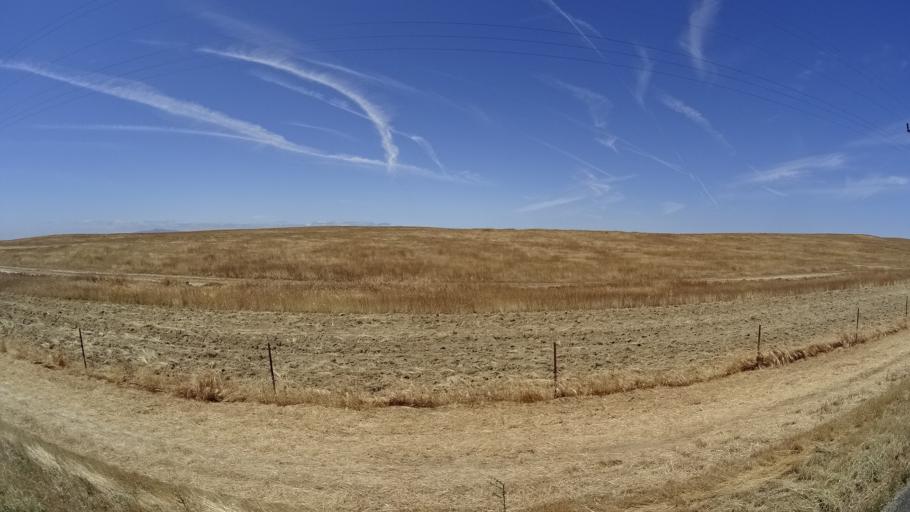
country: US
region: California
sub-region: Kings County
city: Kettleman City
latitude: 35.8610
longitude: -119.9153
